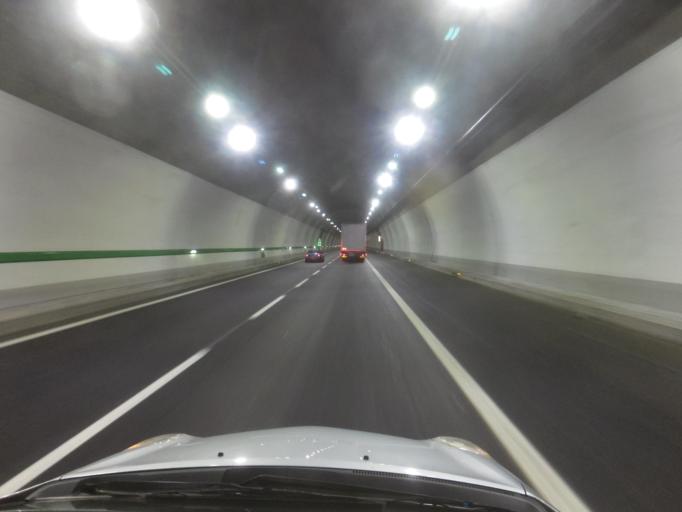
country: IT
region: Tuscany
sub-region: Province of Florence
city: Barberino di Mugello
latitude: 44.0420
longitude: 11.2334
